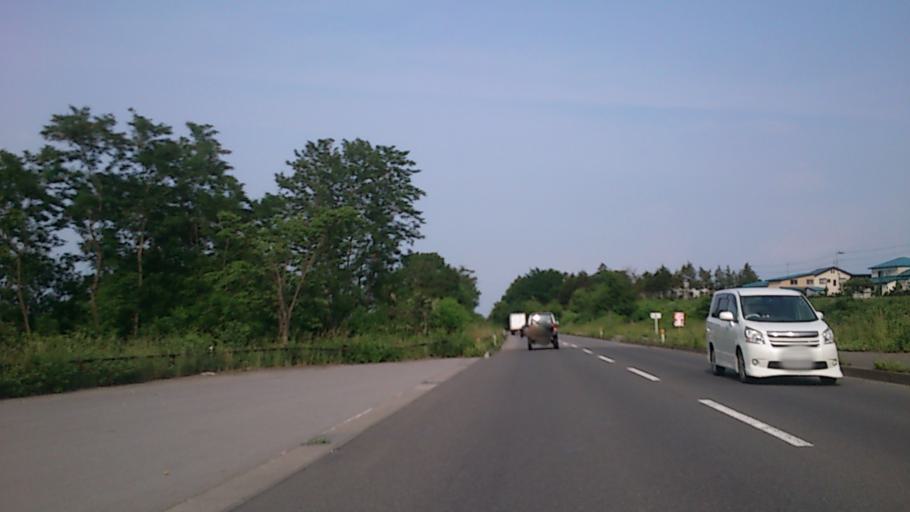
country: JP
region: Aomori
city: Hirosaki
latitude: 40.5905
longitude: 140.4014
